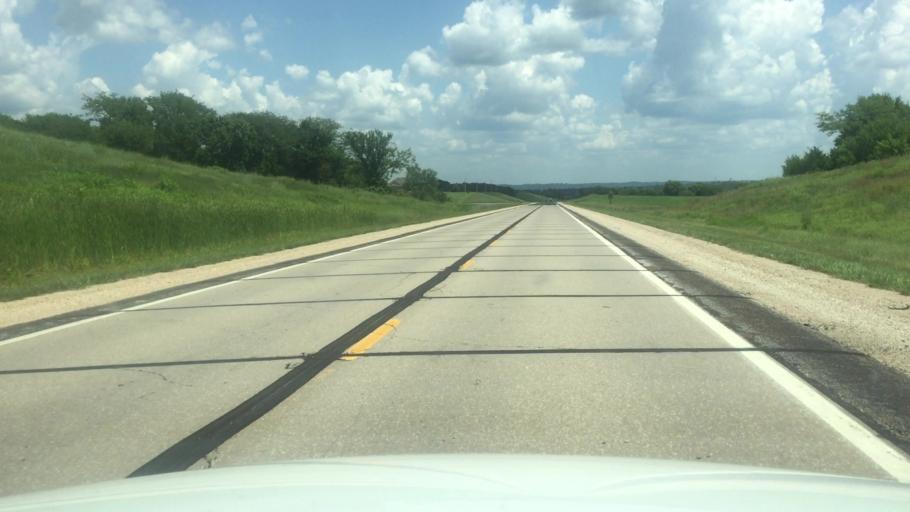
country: US
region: Kansas
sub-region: Atchison County
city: Atchison
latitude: 39.5571
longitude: -95.1759
